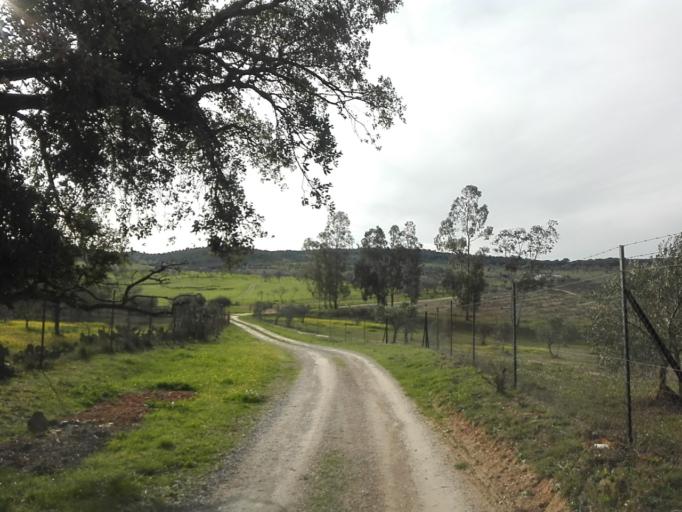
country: ES
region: Extremadura
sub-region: Provincia de Badajoz
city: Llerena
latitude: 38.2193
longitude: -6.0342
